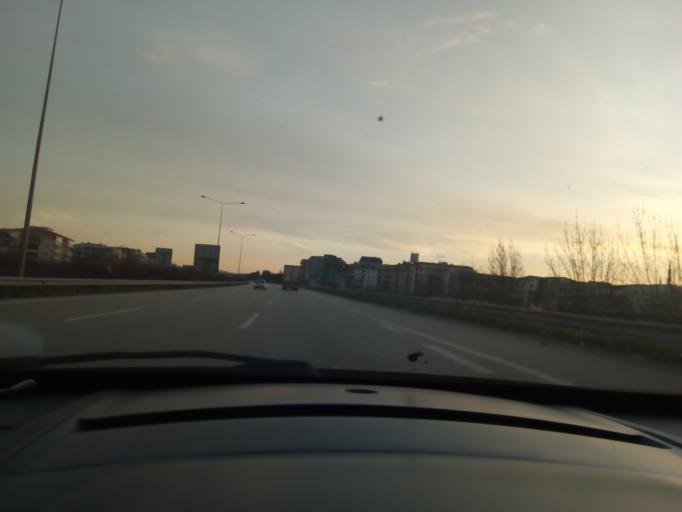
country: TR
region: Bursa
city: Niluefer
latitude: 40.2655
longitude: 28.9521
